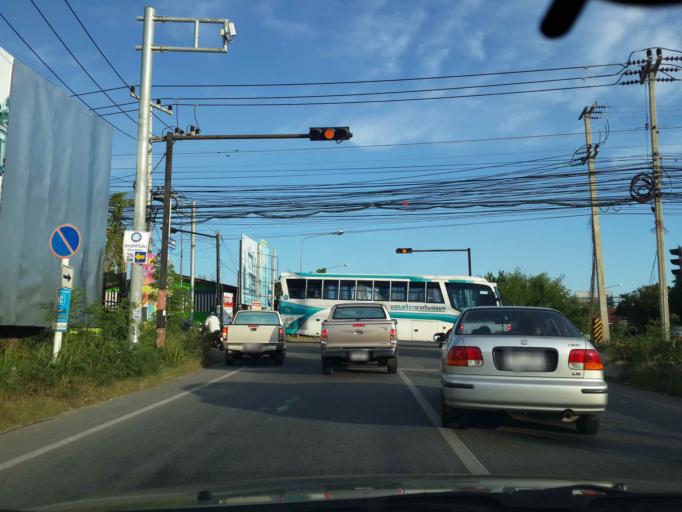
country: TH
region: Chon Buri
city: Phatthaya
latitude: 12.8826
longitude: 100.9045
